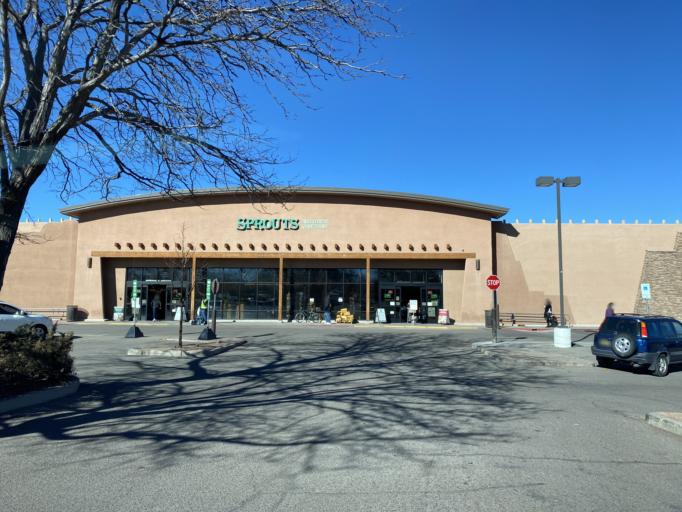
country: US
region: New Mexico
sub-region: Santa Fe County
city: Santa Fe
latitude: 35.6922
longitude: -105.9493
